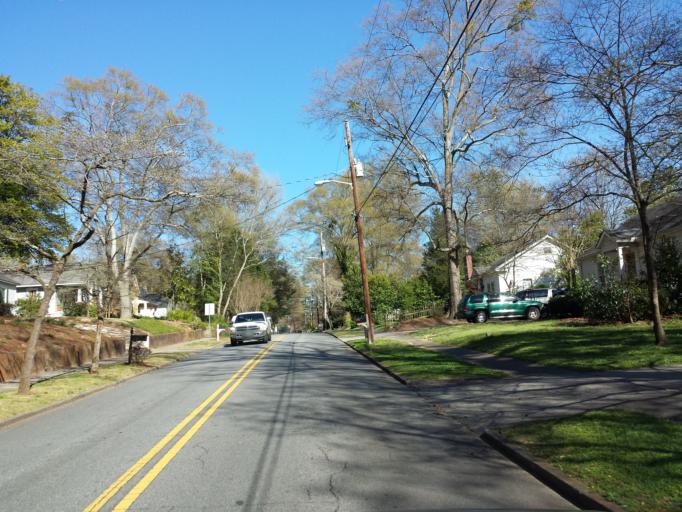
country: US
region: Georgia
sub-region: Cobb County
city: Marietta
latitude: 33.9592
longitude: -84.5583
